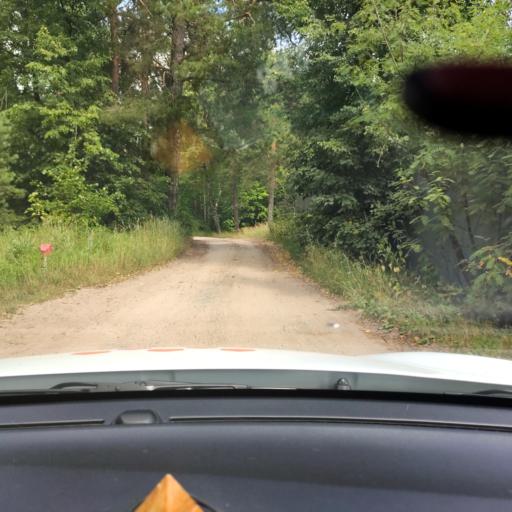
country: RU
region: Tatarstan
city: Osinovo
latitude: 55.9106
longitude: 48.9621
